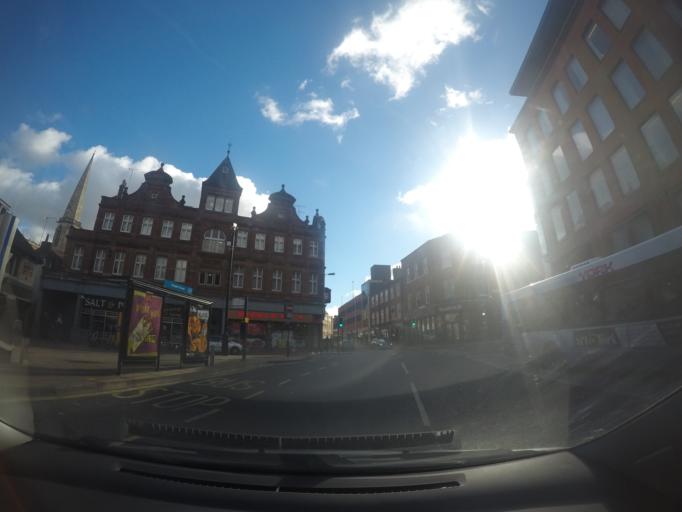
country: GB
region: England
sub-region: City of York
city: York
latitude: 53.9586
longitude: -1.0875
